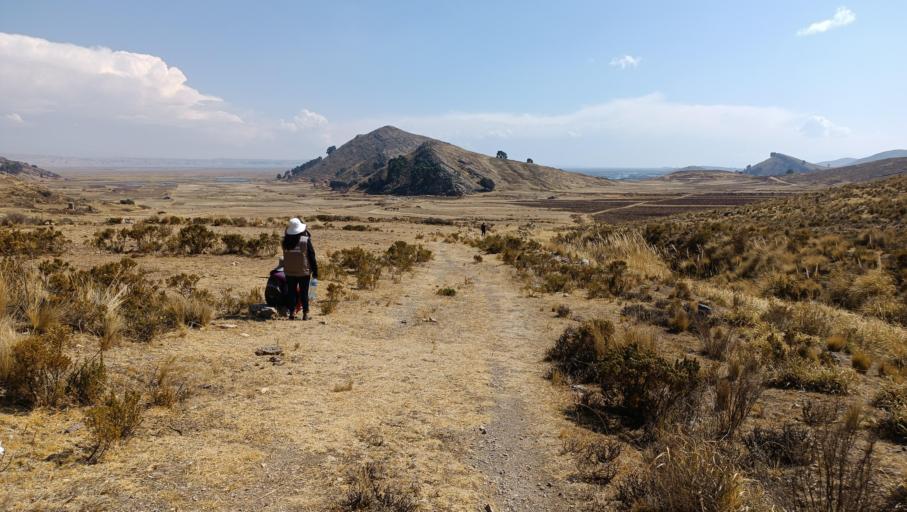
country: BO
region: La Paz
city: Batallas
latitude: -16.3472
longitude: -68.6603
